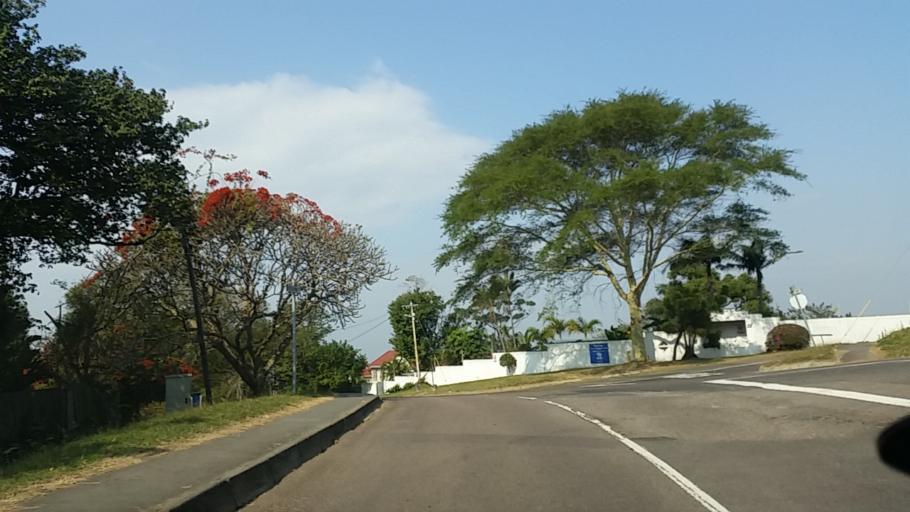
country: ZA
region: KwaZulu-Natal
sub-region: eThekwini Metropolitan Municipality
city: Berea
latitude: -29.8383
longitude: 30.9360
